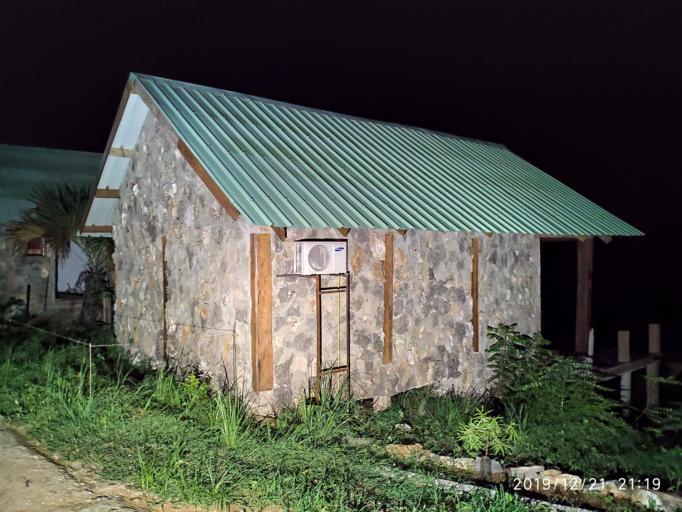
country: MG
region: Diana
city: Ambilobe
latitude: -12.9621
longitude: 49.1501
